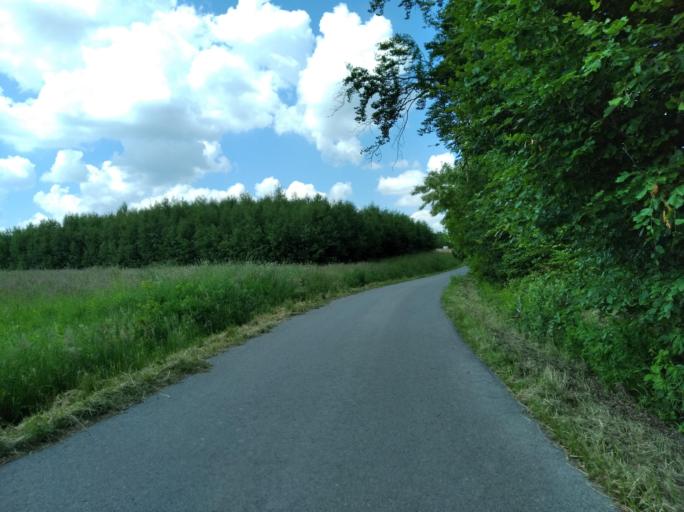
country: PL
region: Subcarpathian Voivodeship
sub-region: Powiat ropczycko-sedziszowski
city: Zagorzyce
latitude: 49.9656
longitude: 21.7157
